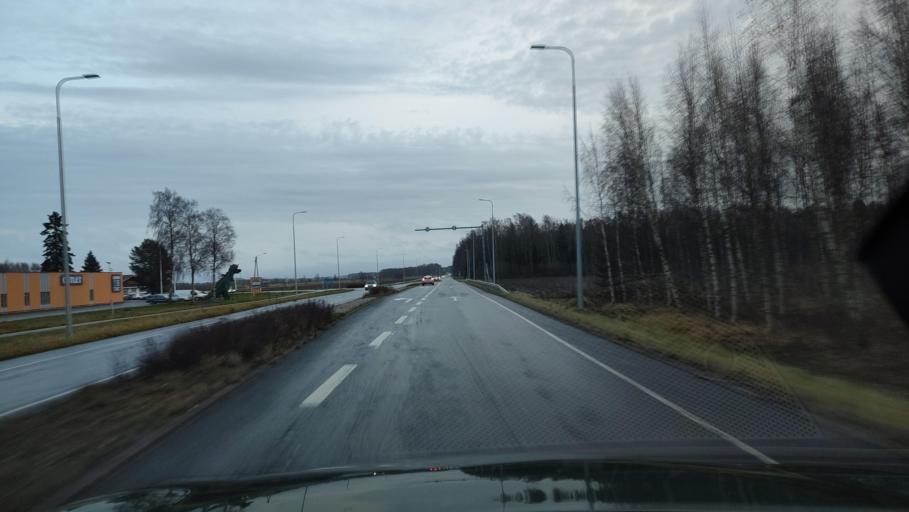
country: FI
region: Ostrobothnia
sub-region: Vaasa
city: Ristinummi
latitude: 63.0492
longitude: 21.7276
